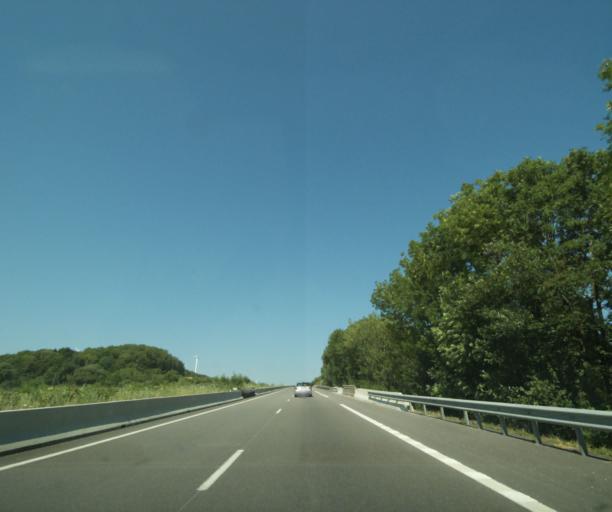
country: FR
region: Lorraine
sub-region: Departement de la Meuse
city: Vacon
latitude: 48.7049
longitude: 5.5253
